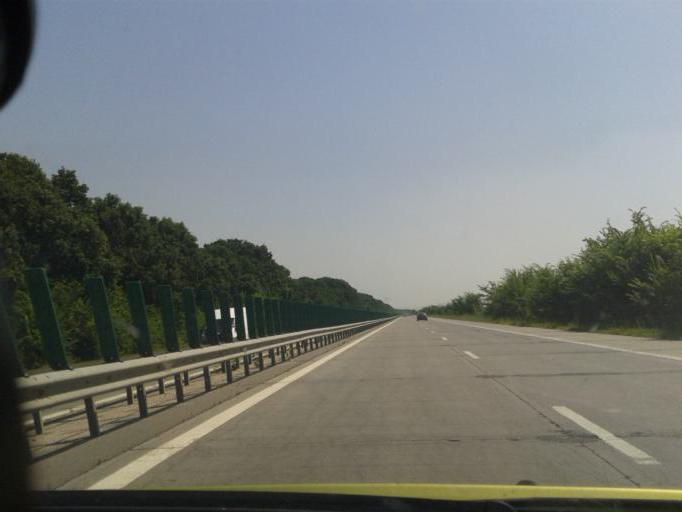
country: RO
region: Calarasi
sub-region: Comuna Belciugatele
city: Belciugatele
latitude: 44.4439
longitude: 26.4263
